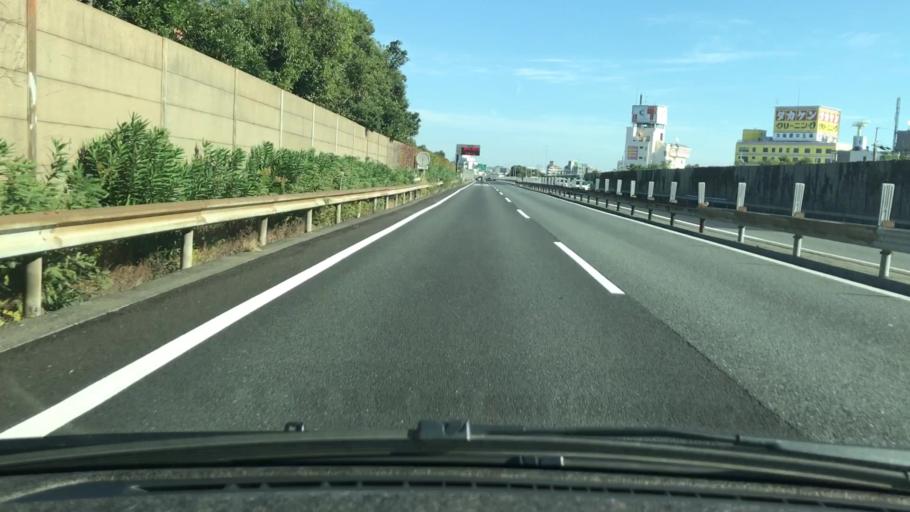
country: JP
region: Osaka
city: Toyonaka
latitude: 34.7506
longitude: 135.4597
